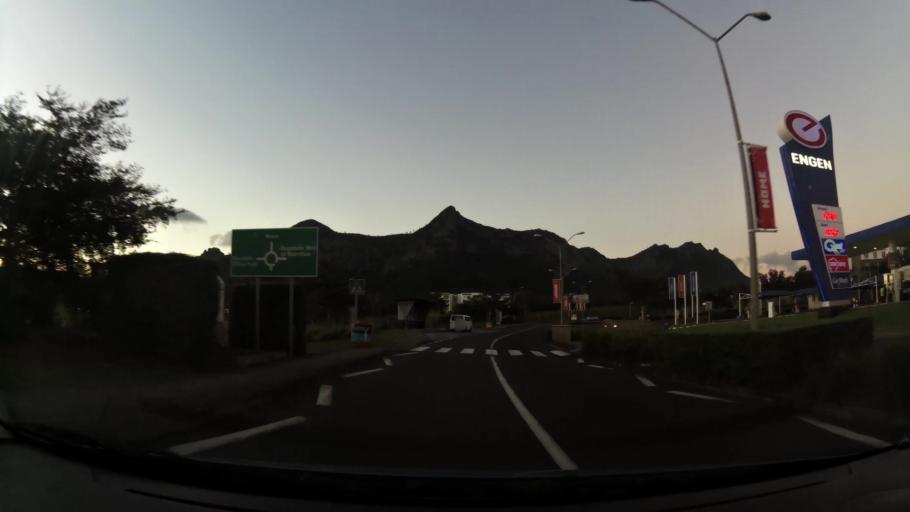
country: MU
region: Moka
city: Moka
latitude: -20.2233
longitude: 57.4938
